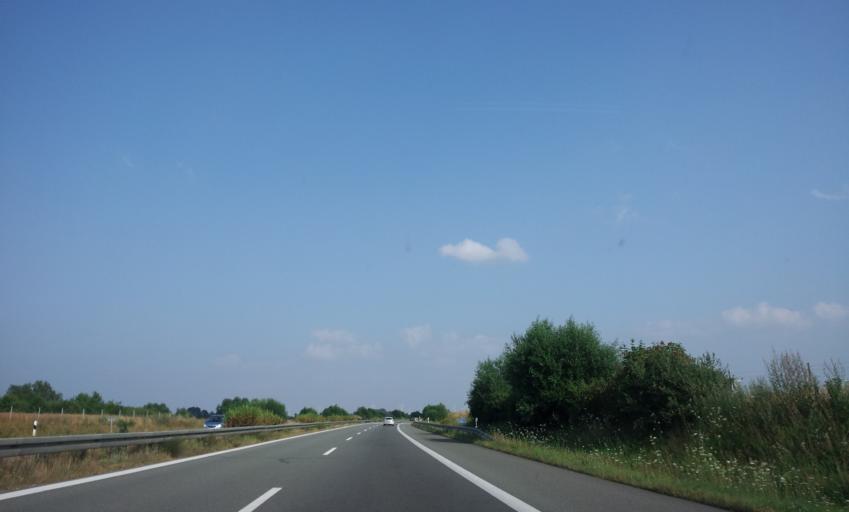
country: DE
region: Mecklenburg-Vorpommern
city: Neuenkirchen
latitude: 53.5752
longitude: 13.4464
